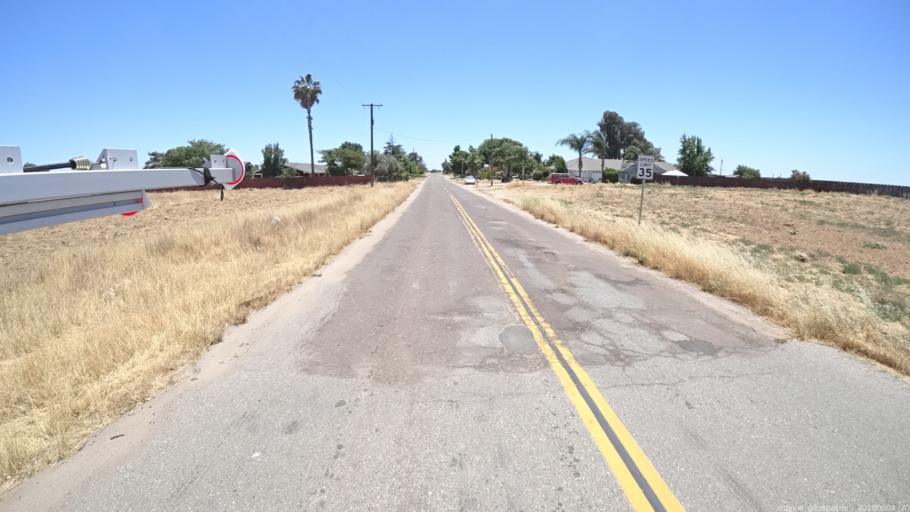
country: US
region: California
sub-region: Madera County
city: Madera Acres
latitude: 36.9962
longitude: -120.0915
